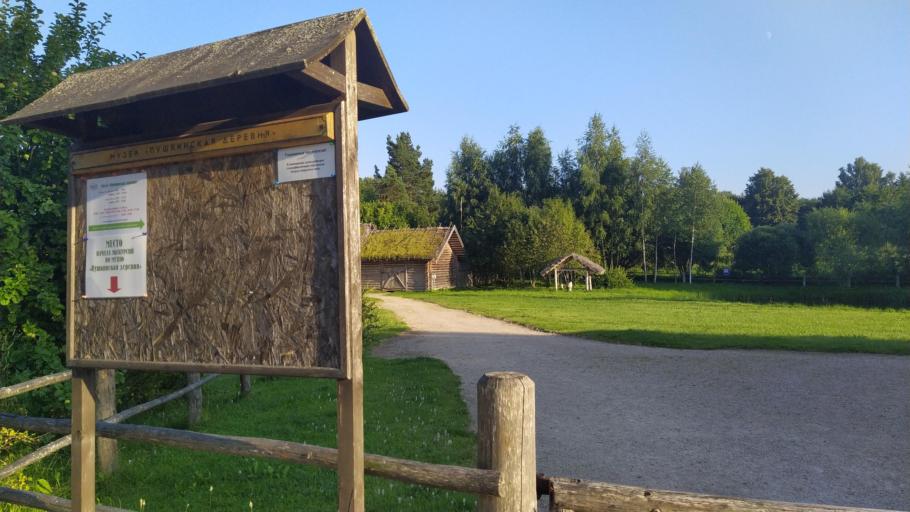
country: RU
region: Pskov
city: Pushkinskiye Gory
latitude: 57.0473
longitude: 28.9162
